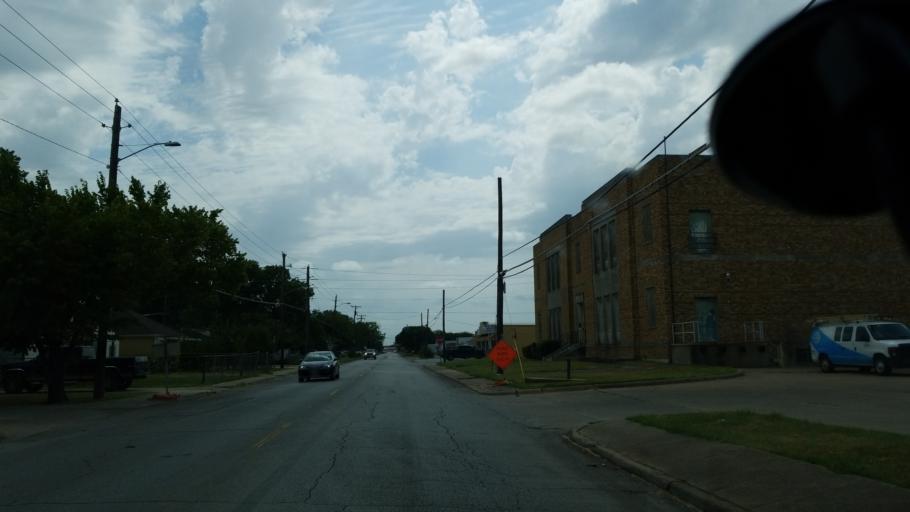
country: US
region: Texas
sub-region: Dallas County
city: Grand Prairie
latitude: 32.7487
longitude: -96.9869
